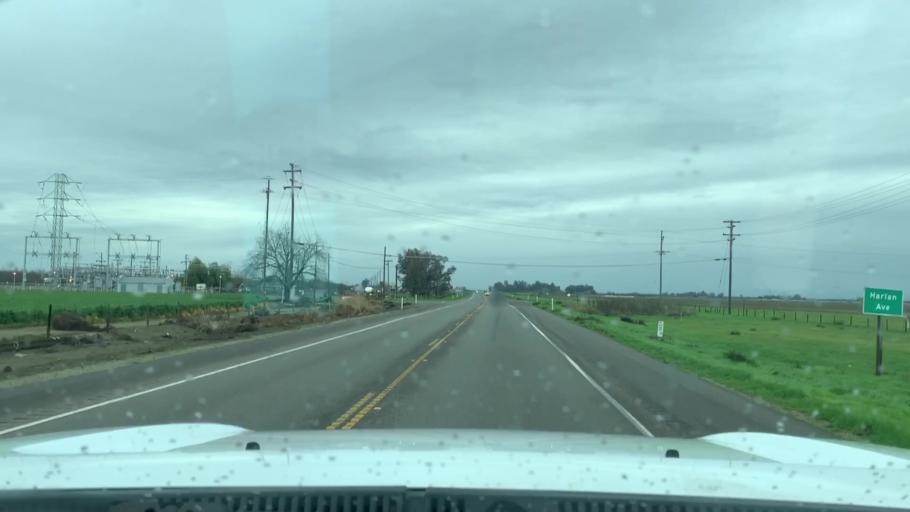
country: US
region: California
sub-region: Fresno County
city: Riverdale
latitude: 36.4445
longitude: -119.7984
